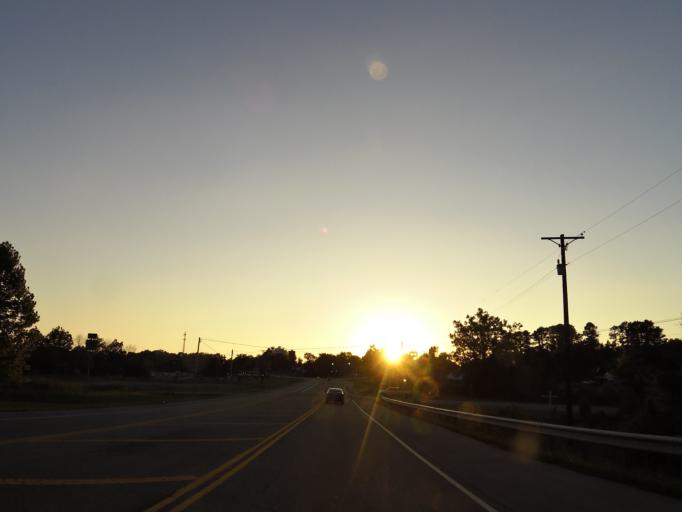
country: US
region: Tennessee
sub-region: Knox County
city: Mascot
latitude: 36.0255
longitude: -83.7262
